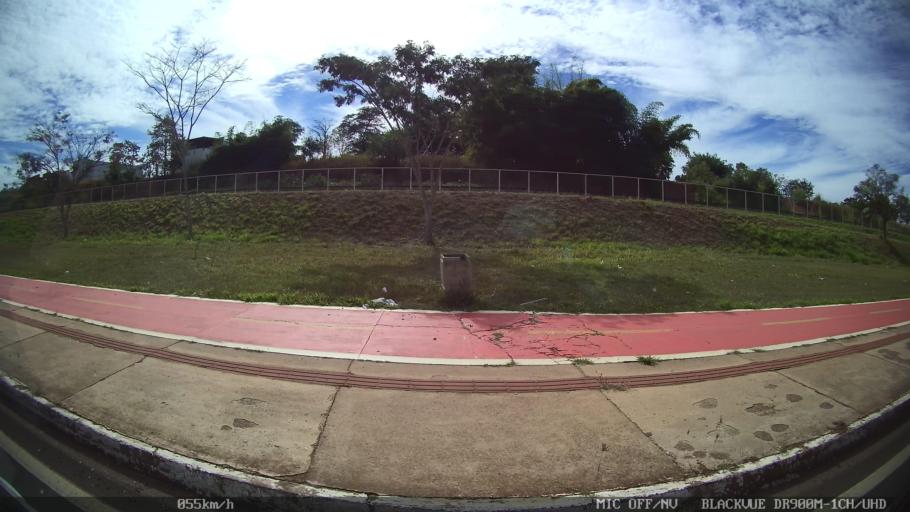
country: BR
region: Sao Paulo
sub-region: Catanduva
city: Catanduva
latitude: -21.1418
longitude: -48.9540
